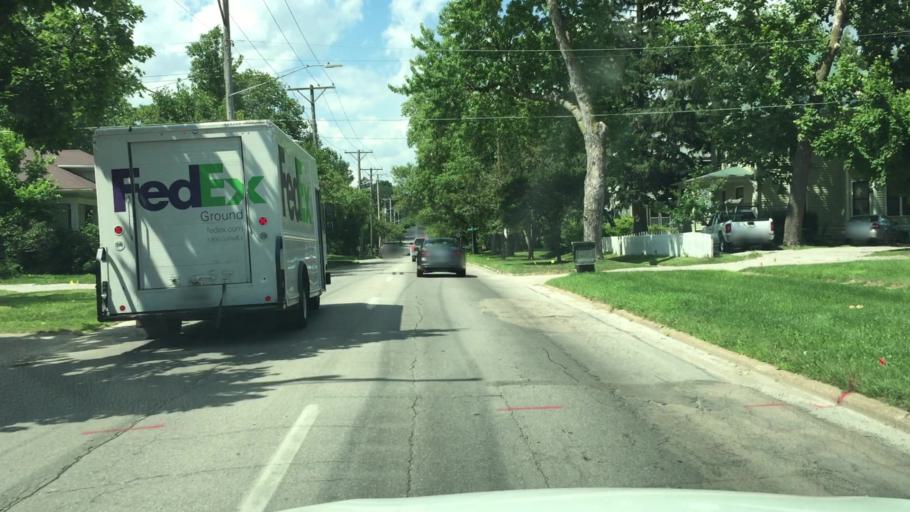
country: US
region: Iowa
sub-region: Johnson County
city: Iowa City
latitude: 41.6638
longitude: -91.5228
